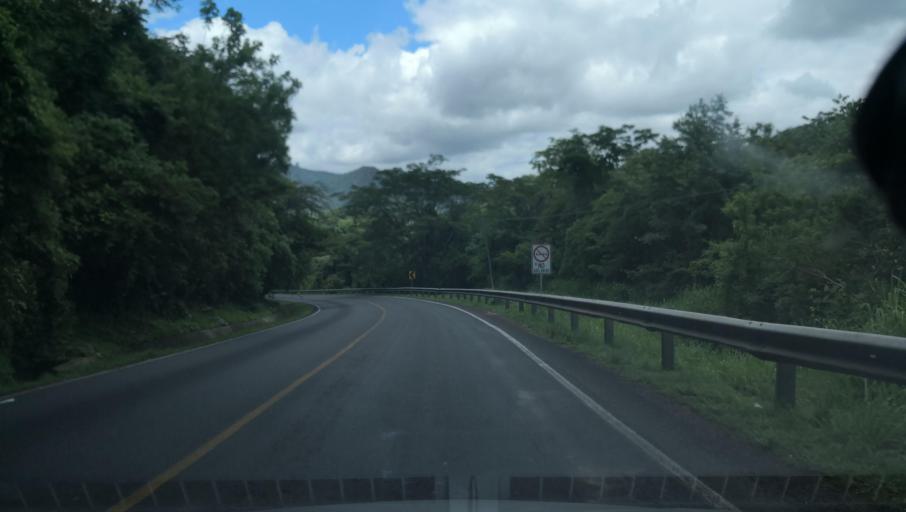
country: NI
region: Esteli
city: Condega
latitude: 13.2499
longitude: -86.3584
